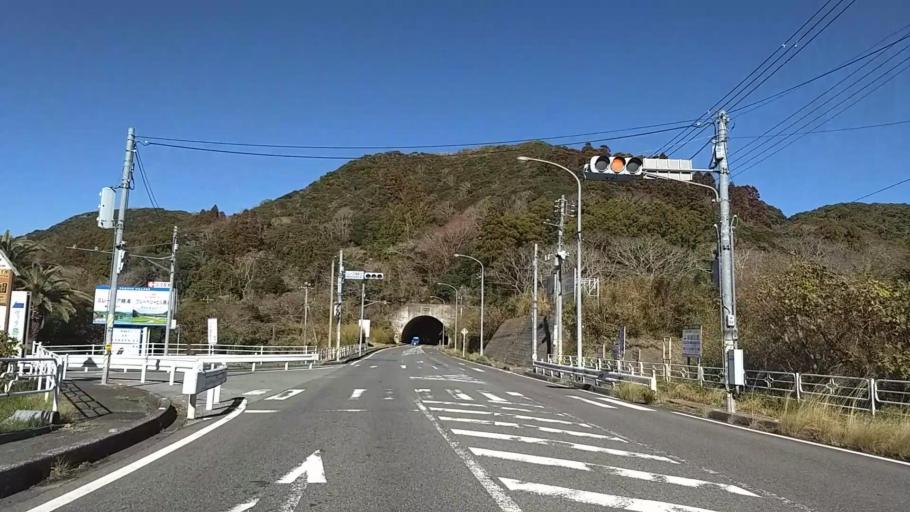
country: JP
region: Chiba
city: Katsuura
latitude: 35.1317
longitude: 140.2407
